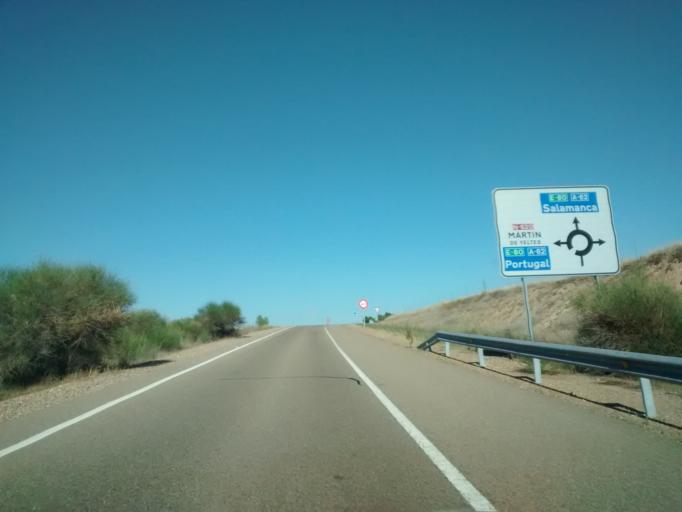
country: ES
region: Castille and Leon
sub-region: Provincia de Salamanca
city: Martin de Yeltes
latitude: 40.7708
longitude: -6.2864
